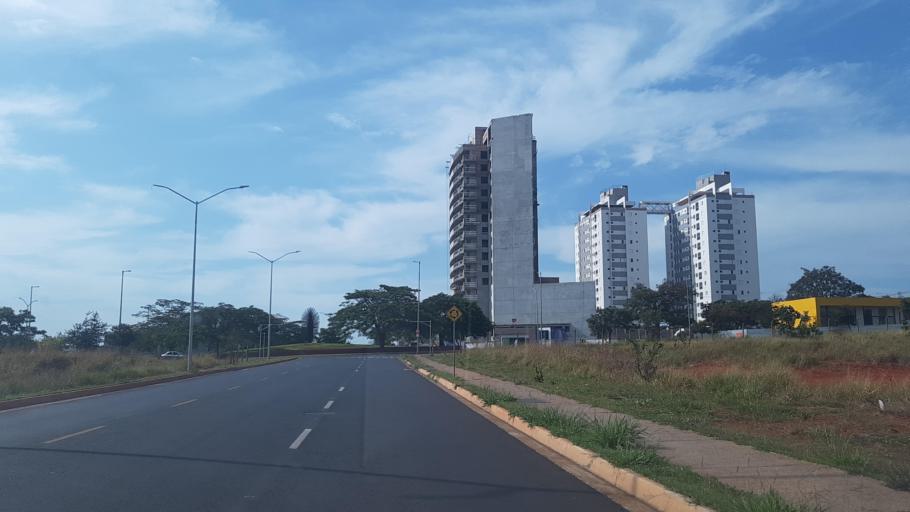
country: BR
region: Minas Gerais
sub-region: Uberlandia
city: Uberlandia
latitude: -18.8785
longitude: -48.2495
